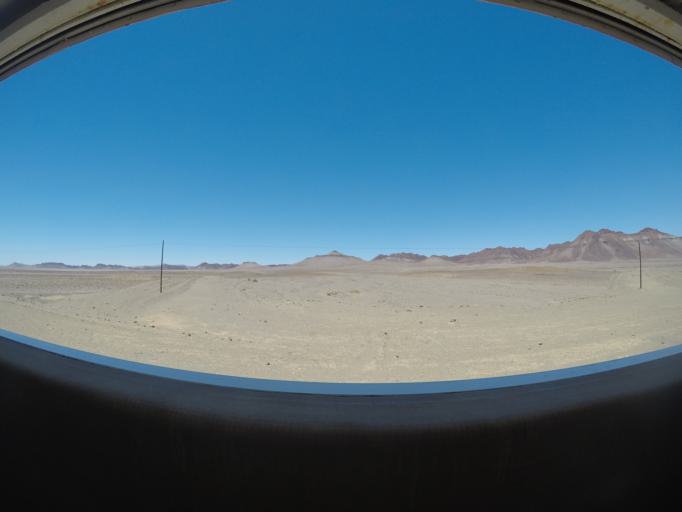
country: ZA
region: Northern Cape
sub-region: Namakwa District Municipality
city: Port Nolloth
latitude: -28.6018
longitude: 17.4853
